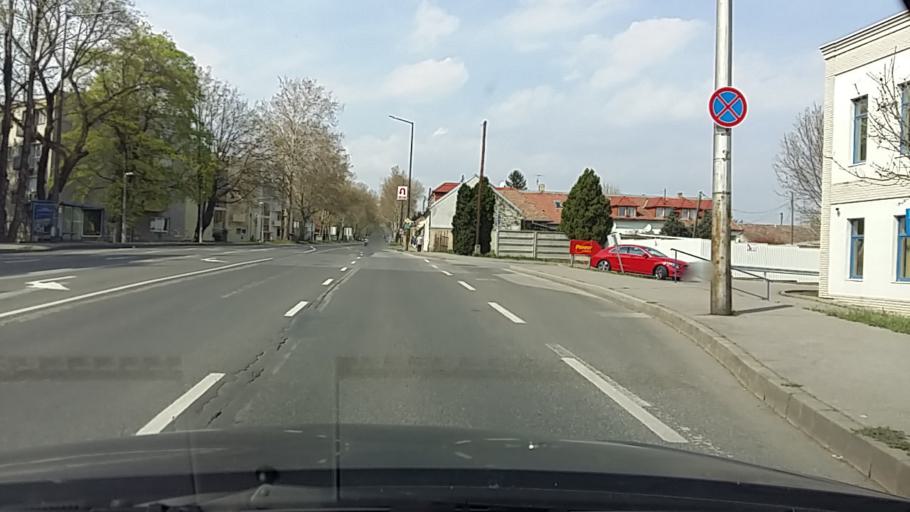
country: HU
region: Baranya
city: Pecs
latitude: 46.0862
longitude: 18.2704
